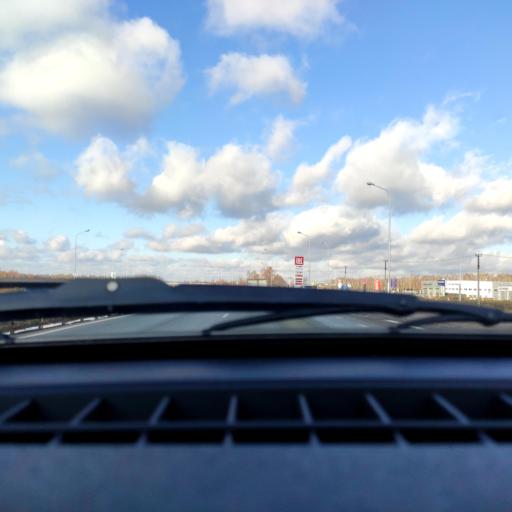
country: RU
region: Bashkortostan
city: Kabakovo
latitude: 54.6580
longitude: 56.0817
